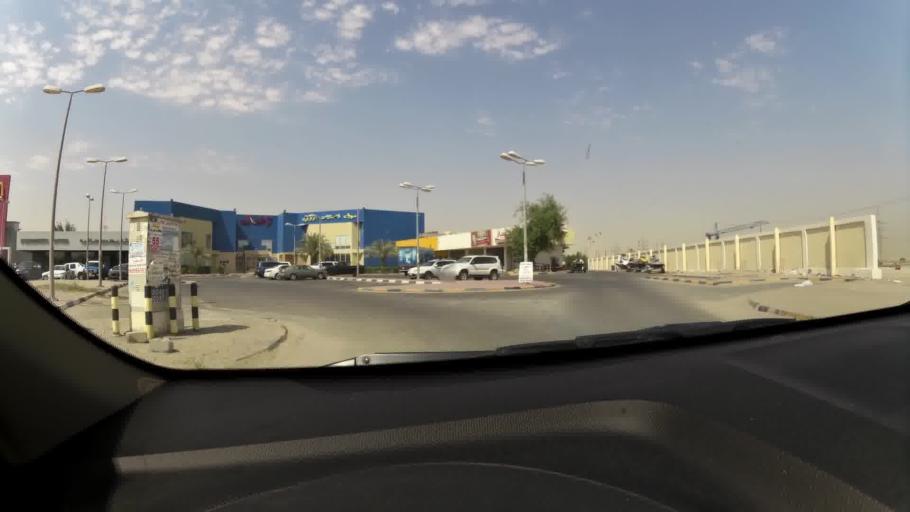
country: SA
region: Eastern Province
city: Al Khafji
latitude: 28.7318
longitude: 48.2852
